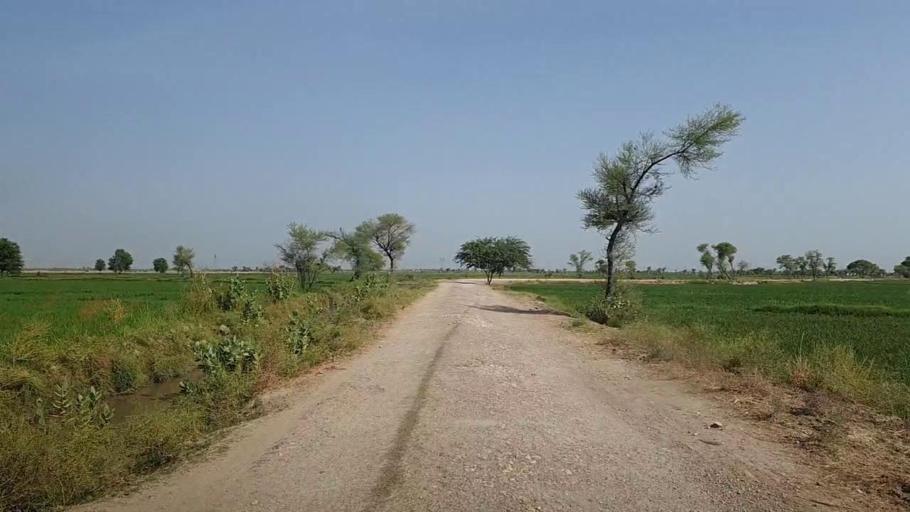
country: PK
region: Sindh
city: Sita Road
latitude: 27.1048
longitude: 67.8521
